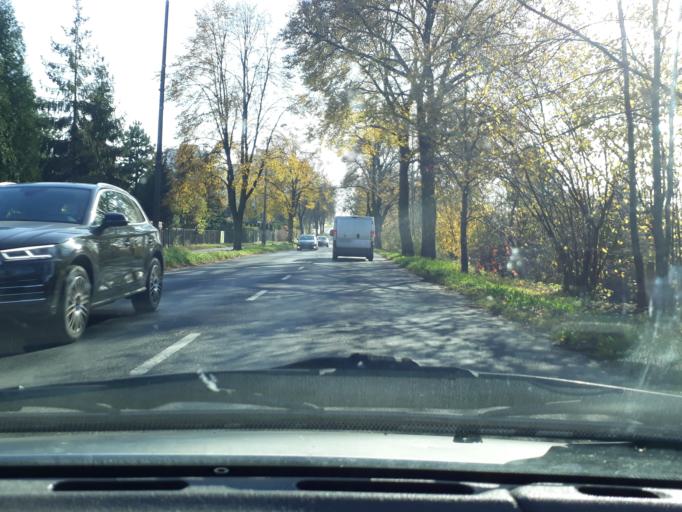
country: PL
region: Silesian Voivodeship
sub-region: Powiat tarnogorski
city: Tarnowskie Gory
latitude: 50.4356
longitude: 18.8634
